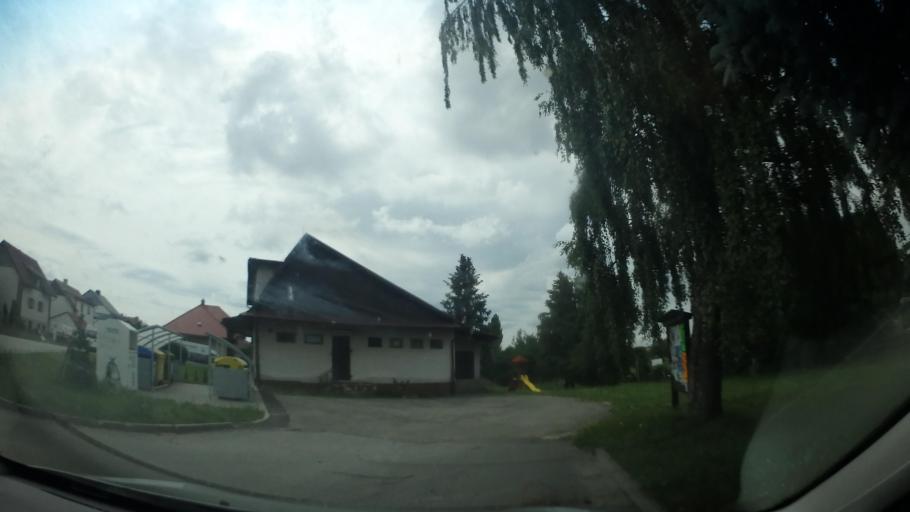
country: CZ
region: Vysocina
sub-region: Okres Zd'ar nad Sazavou
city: Nove Mesto na Morave
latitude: 49.5789
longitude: 16.0787
